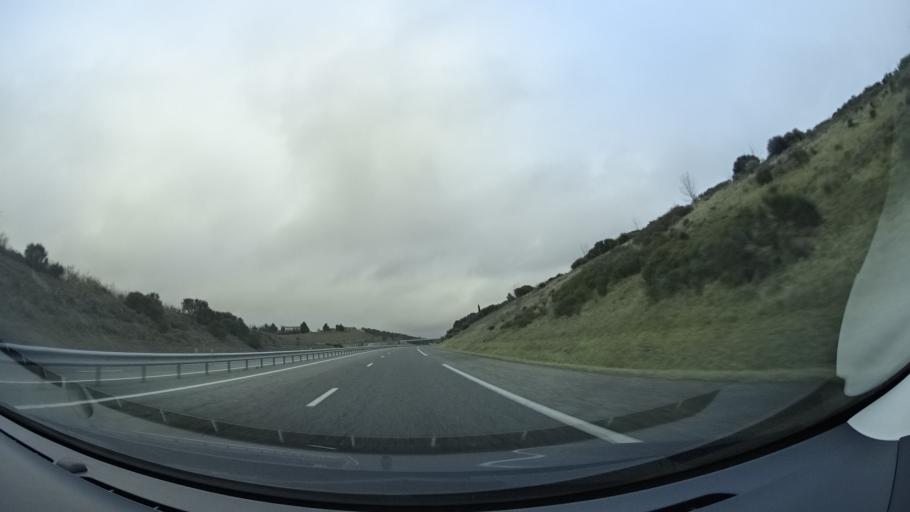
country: FR
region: Midi-Pyrenees
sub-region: Departement de la Haute-Garonne
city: Nailloux
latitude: 43.3661
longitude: 1.5957
